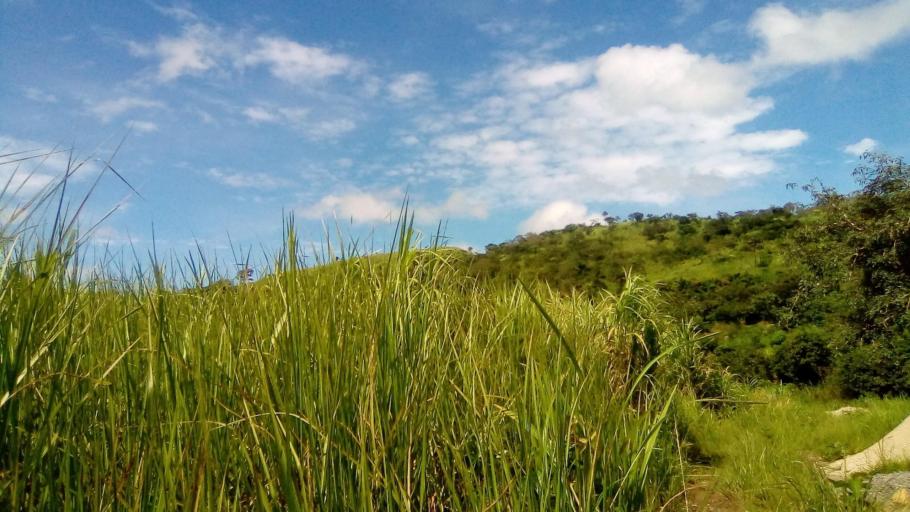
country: SL
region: Eastern Province
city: Simbakoro
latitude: 8.6356
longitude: -11.0017
